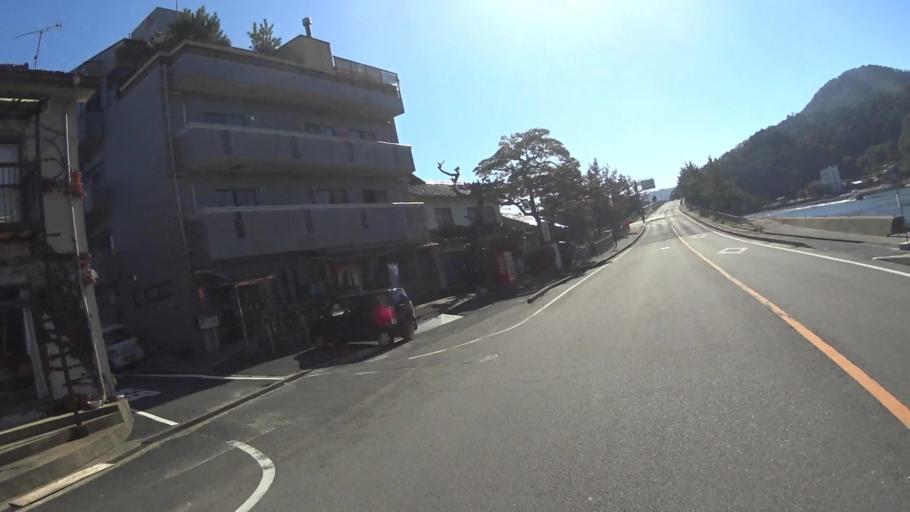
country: JP
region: Hyogo
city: Toyooka
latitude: 35.6443
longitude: 134.9022
